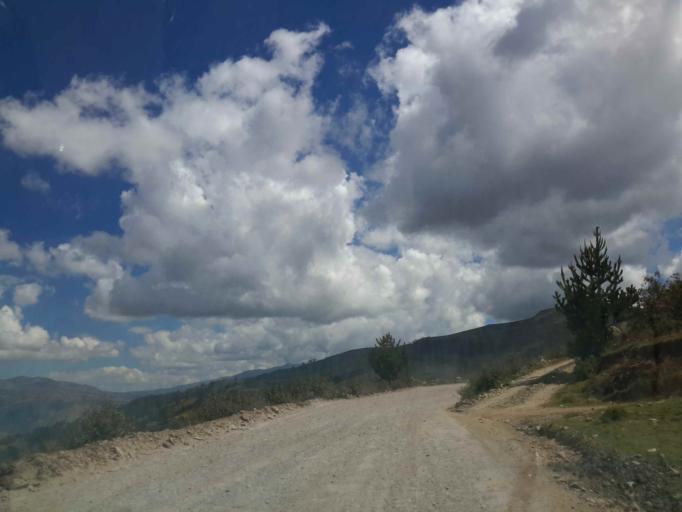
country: PE
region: Apurimac
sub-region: Provincia de Andahuaylas
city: San Jeronimo
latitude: -13.6377
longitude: -73.3385
